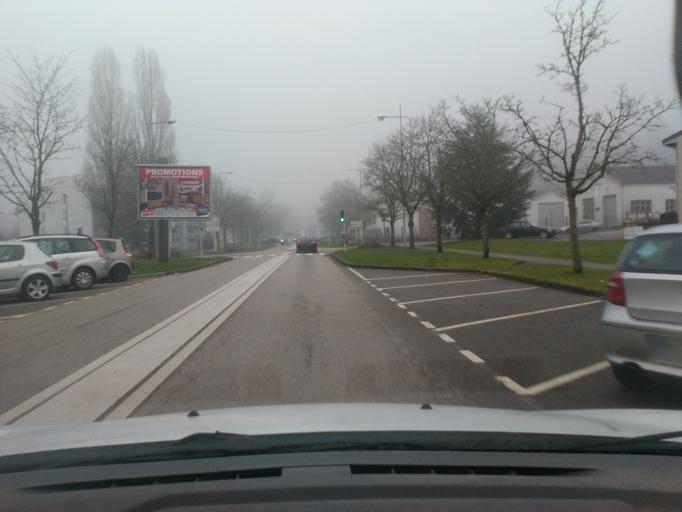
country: FR
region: Lorraine
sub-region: Departement des Vosges
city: Epinal
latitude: 48.1909
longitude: 6.4592
